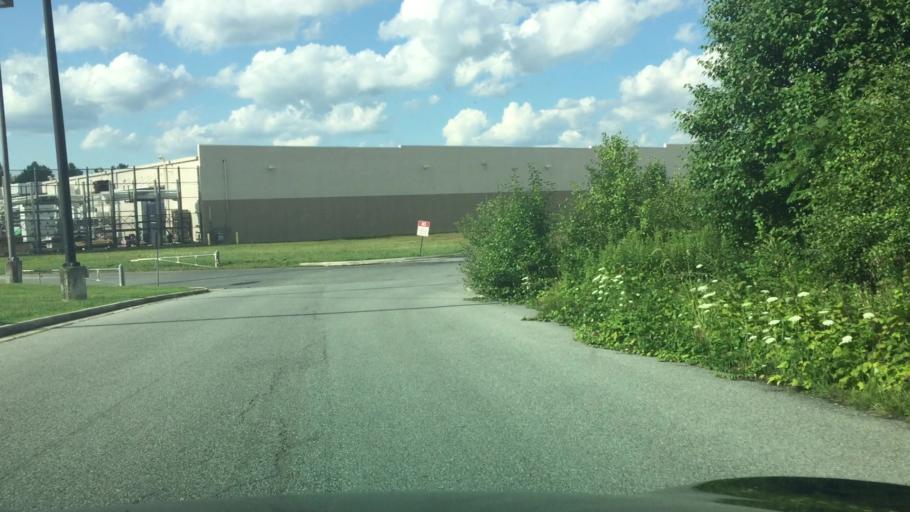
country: US
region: Virginia
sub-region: Wythe County
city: Wytheville
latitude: 36.9558
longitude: -81.1028
